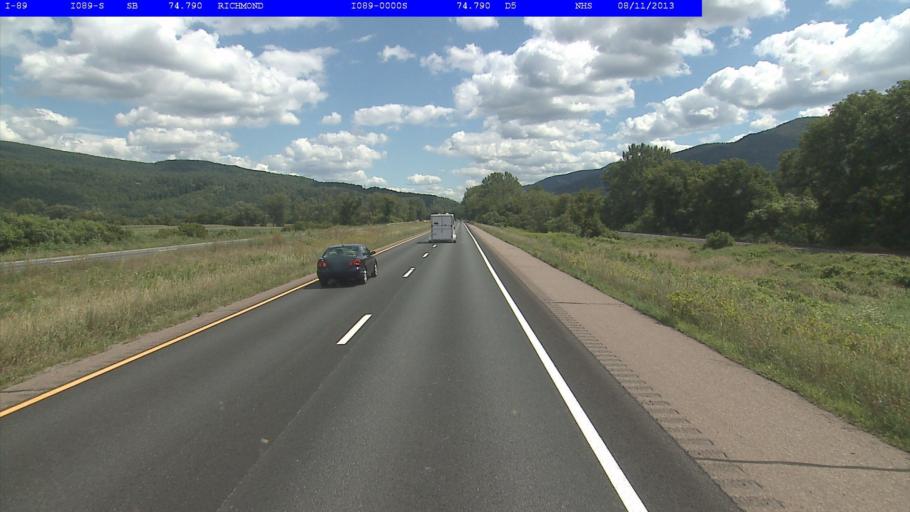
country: US
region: Vermont
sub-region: Chittenden County
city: Jericho
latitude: 44.3922
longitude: -72.9582
